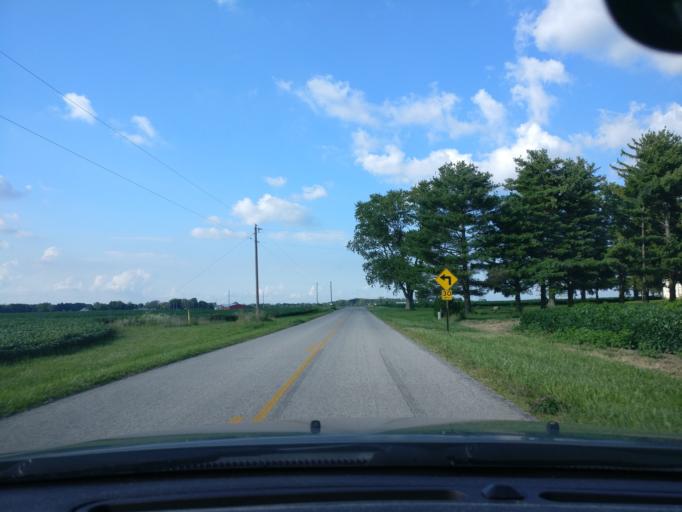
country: US
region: Ohio
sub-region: Clinton County
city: Wilmington
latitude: 39.5309
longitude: -83.8334
